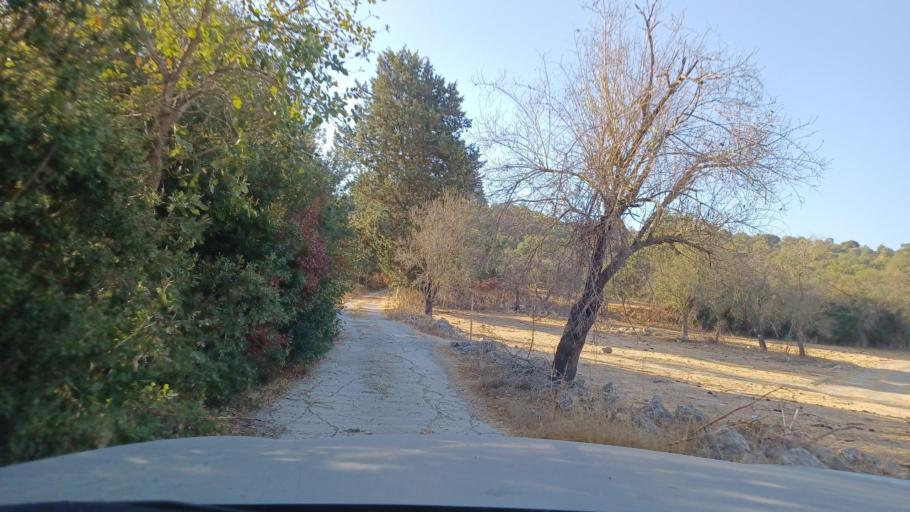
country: CY
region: Pafos
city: Polis
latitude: 34.9962
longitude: 32.4878
